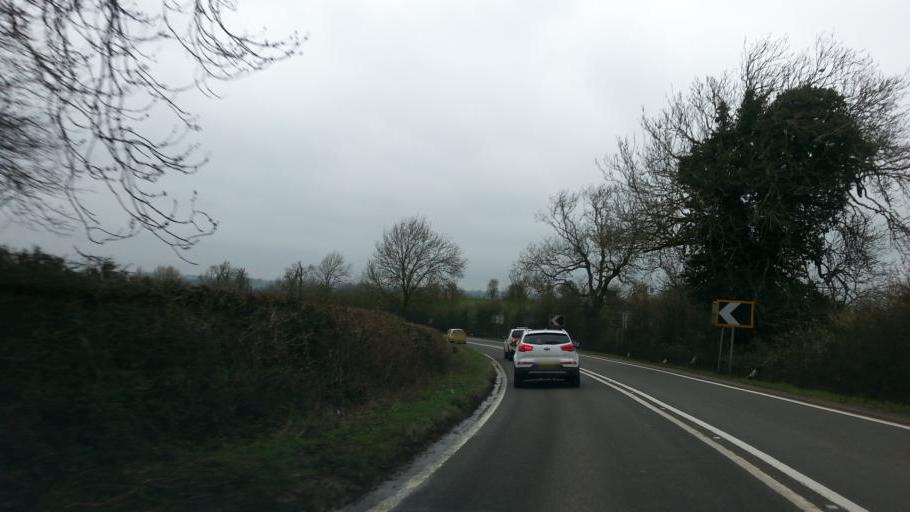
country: GB
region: England
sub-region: Northamptonshire
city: Brackley
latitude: 52.0555
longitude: -1.2250
